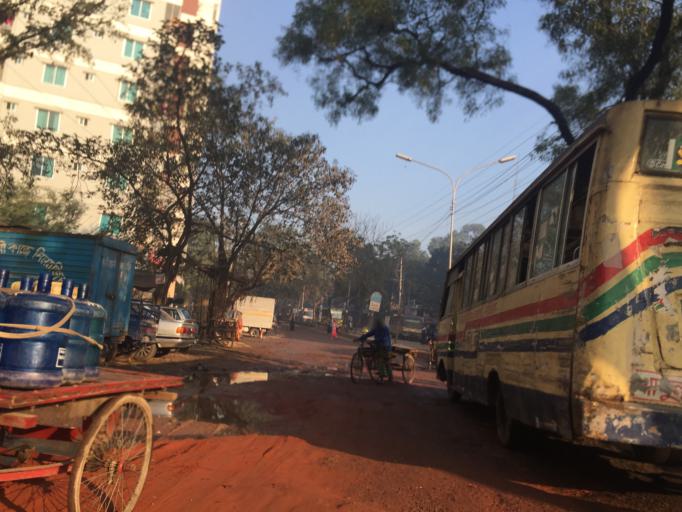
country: BD
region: Dhaka
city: Azimpur
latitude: 23.8066
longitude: 90.3514
